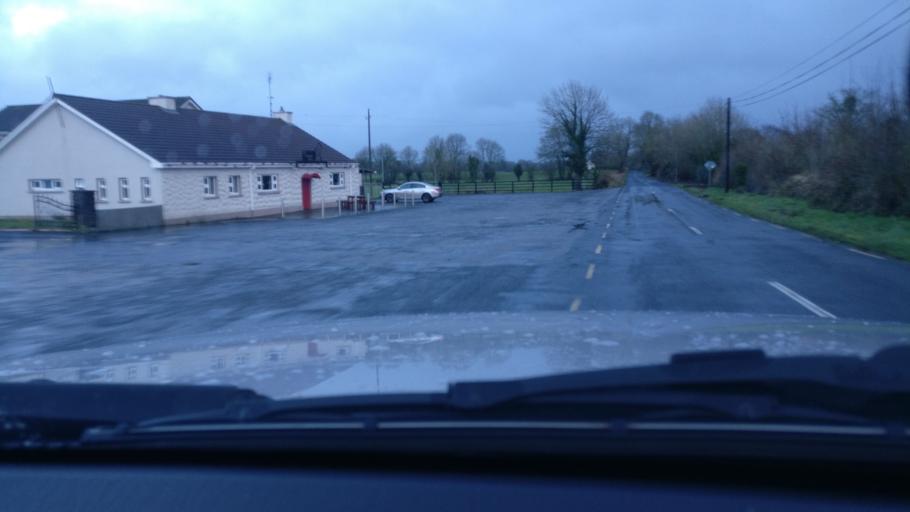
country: IE
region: Connaught
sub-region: County Galway
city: Ballinasloe
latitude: 53.2287
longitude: -8.3486
